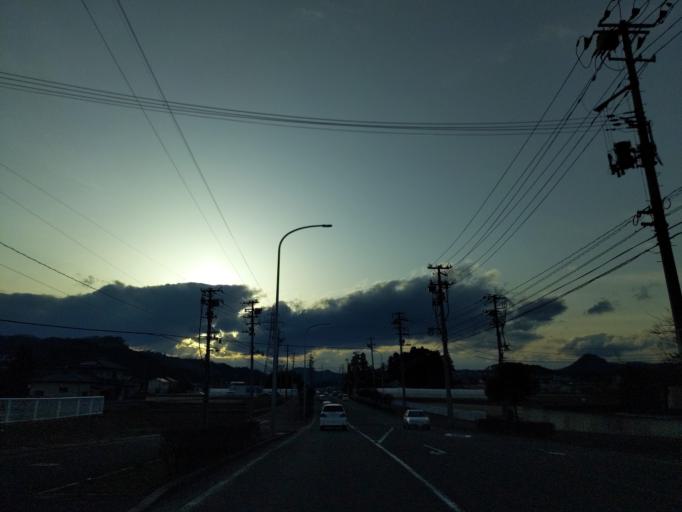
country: JP
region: Miyagi
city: Sendai
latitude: 38.2137
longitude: 140.8453
